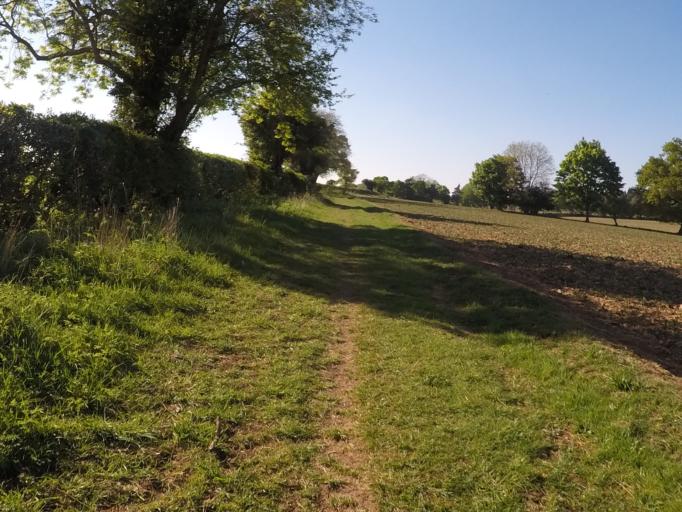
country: GB
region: England
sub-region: Oxfordshire
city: Stonesfield
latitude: 51.8677
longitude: -1.4348
